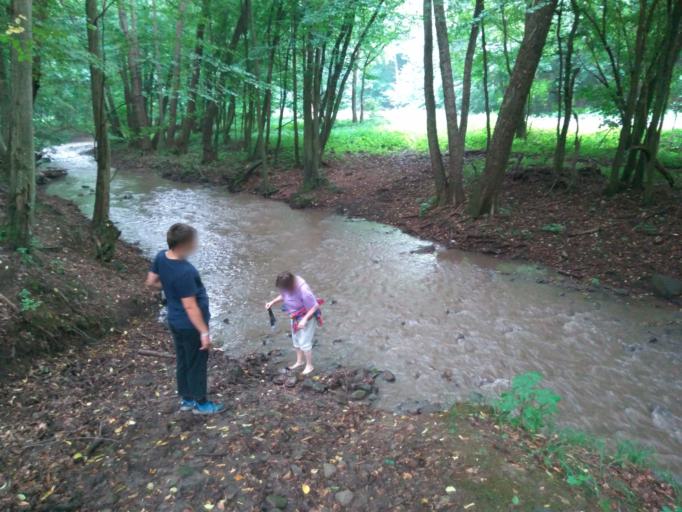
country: HU
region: Nograd
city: Diosjeno
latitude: 47.9847
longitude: 18.9748
